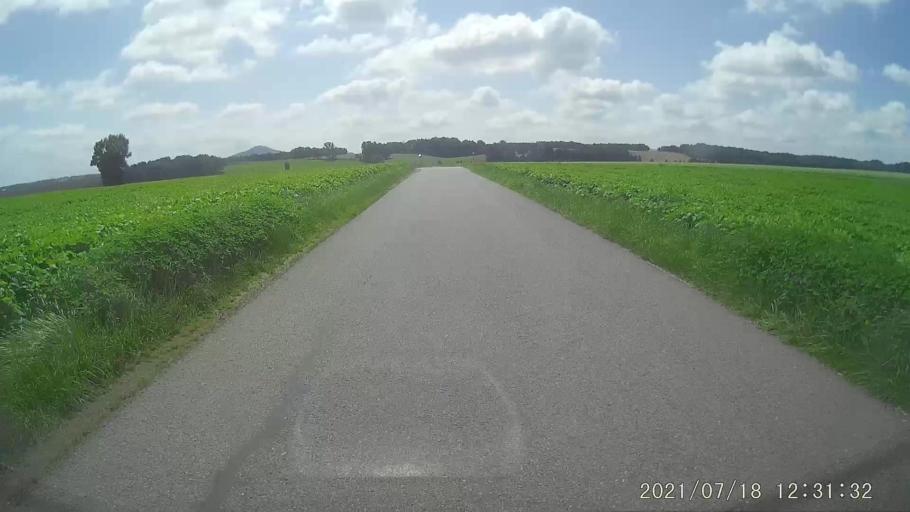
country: DE
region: Saxony
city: Konigshain
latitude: 51.1770
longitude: 14.8977
